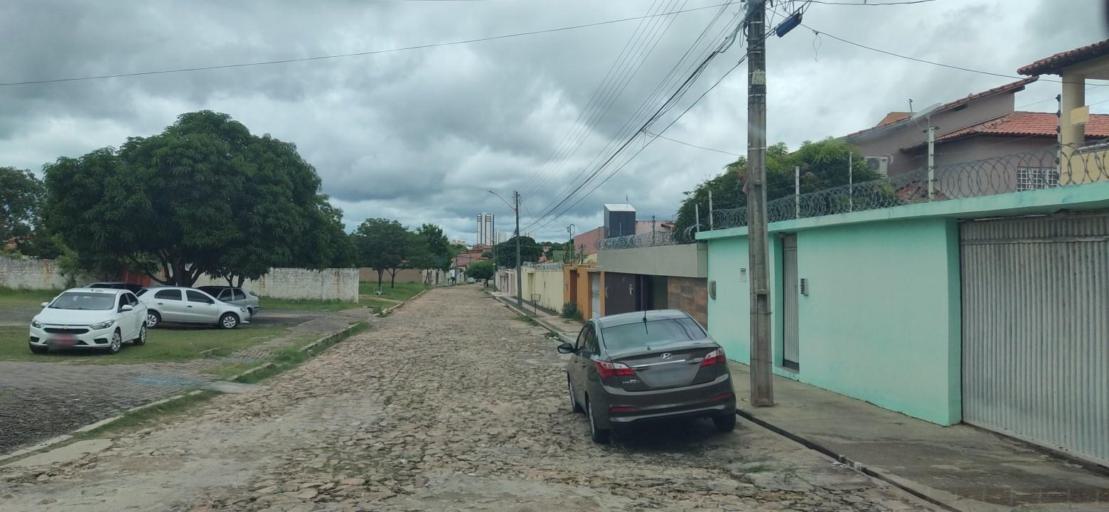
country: BR
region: Piaui
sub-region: Teresina
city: Teresina
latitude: -5.0711
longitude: -42.7589
